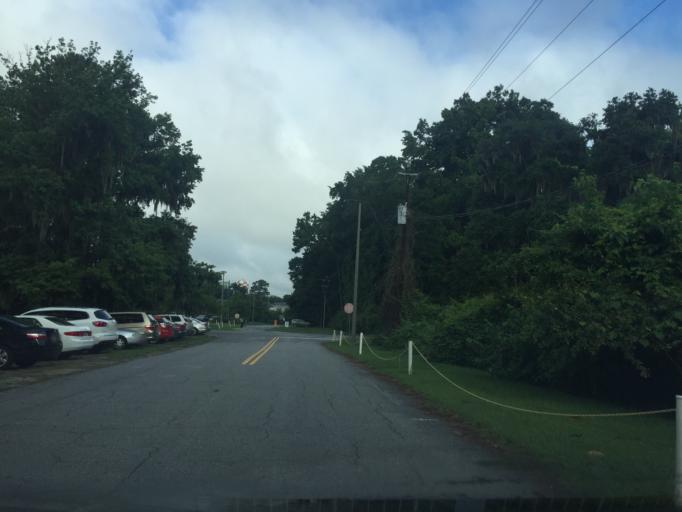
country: US
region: Georgia
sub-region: Chatham County
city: Savannah
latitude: 32.0249
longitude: -81.1147
